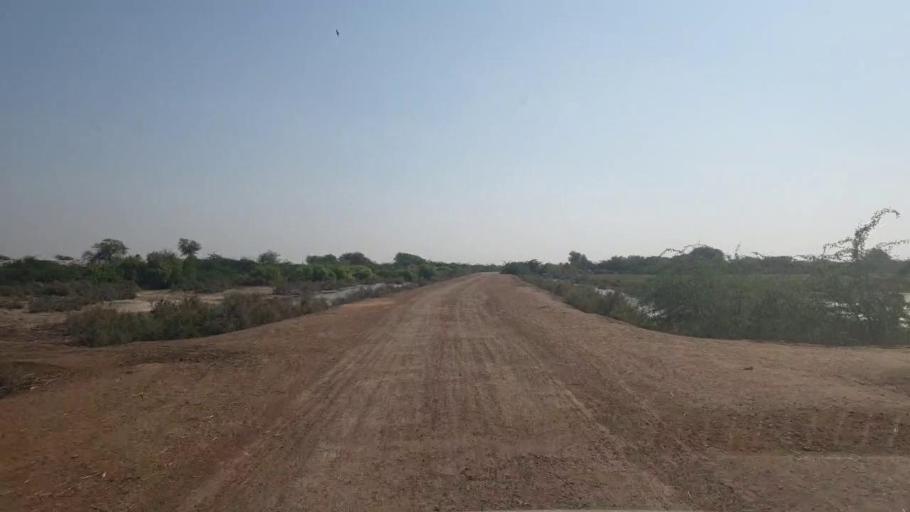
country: PK
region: Sindh
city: Badin
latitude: 24.5640
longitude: 68.8453
